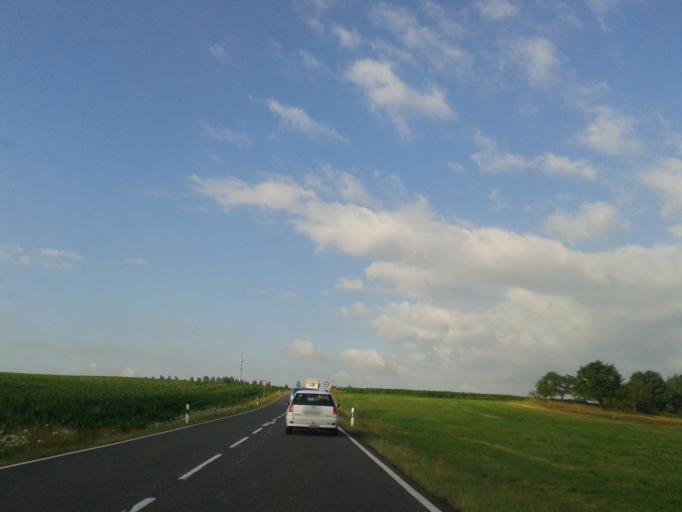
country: DE
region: Saxony
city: Niederschona
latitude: 50.9735
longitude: 13.4377
